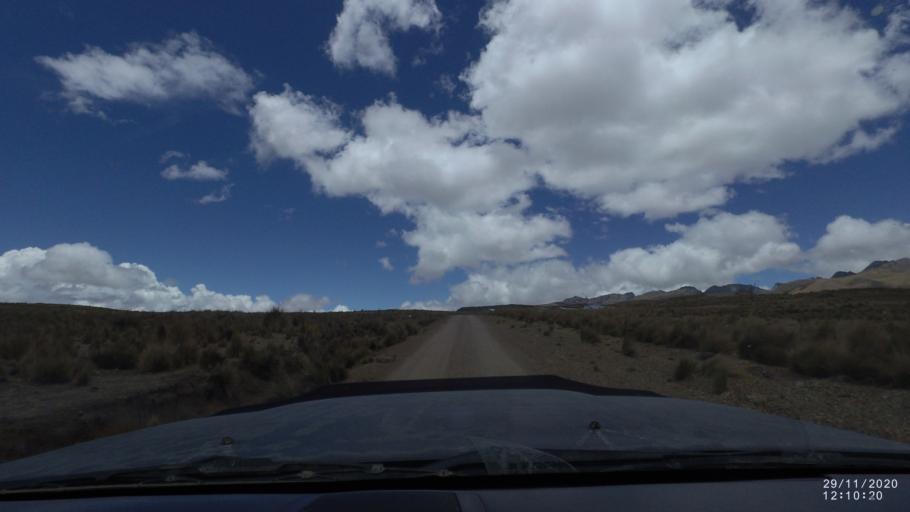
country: BO
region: Cochabamba
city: Cochabamba
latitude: -17.1264
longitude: -66.3068
